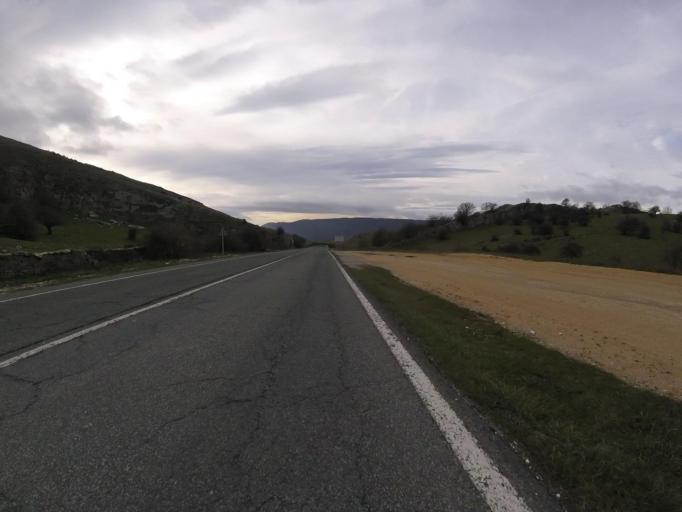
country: ES
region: Navarre
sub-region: Provincia de Navarra
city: Arbizu
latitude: 42.8589
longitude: -2.0120
